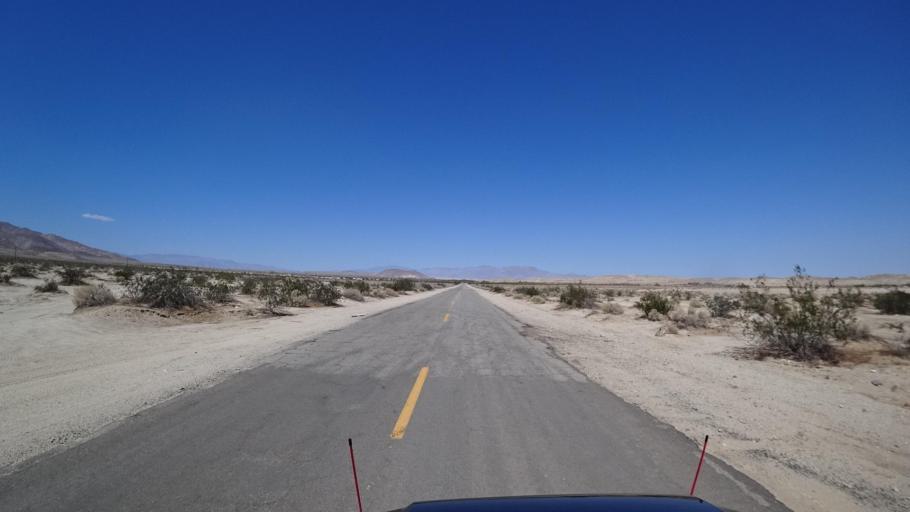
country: US
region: California
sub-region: Imperial County
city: Salton City
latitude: 33.0895
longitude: -116.1110
